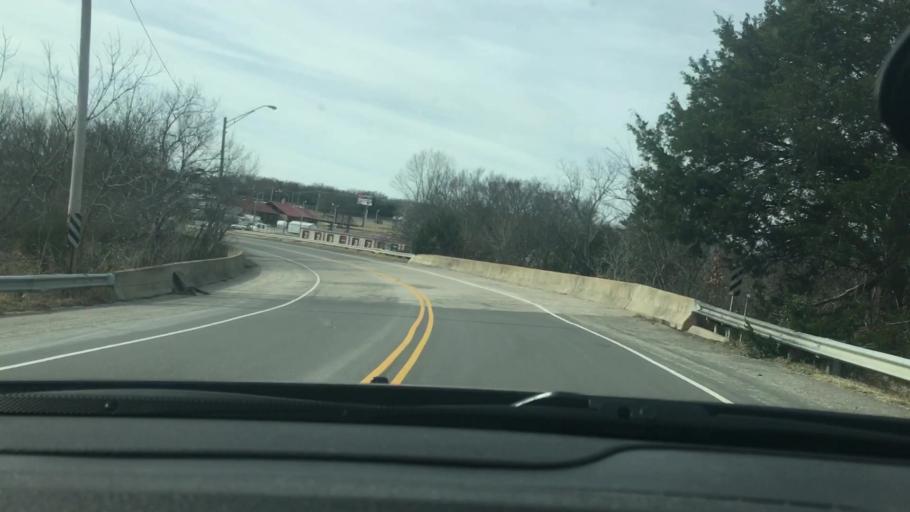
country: US
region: Oklahoma
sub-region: Carter County
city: Ardmore
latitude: 34.1749
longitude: -97.1753
